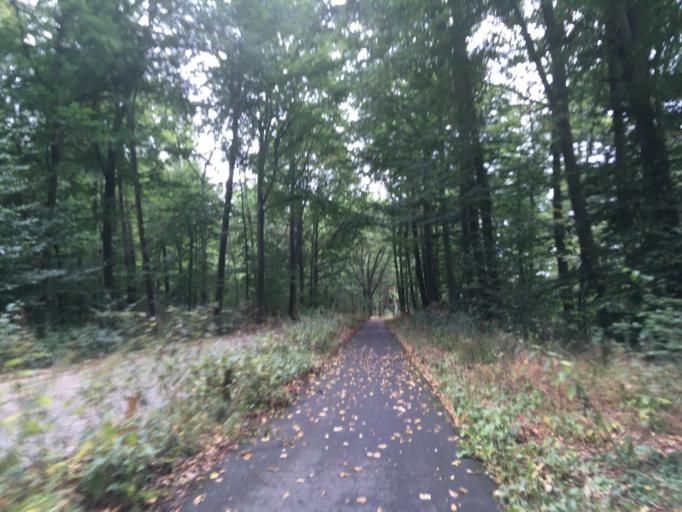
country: DE
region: Brandenburg
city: Chorin
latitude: 52.9084
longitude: 13.8556
